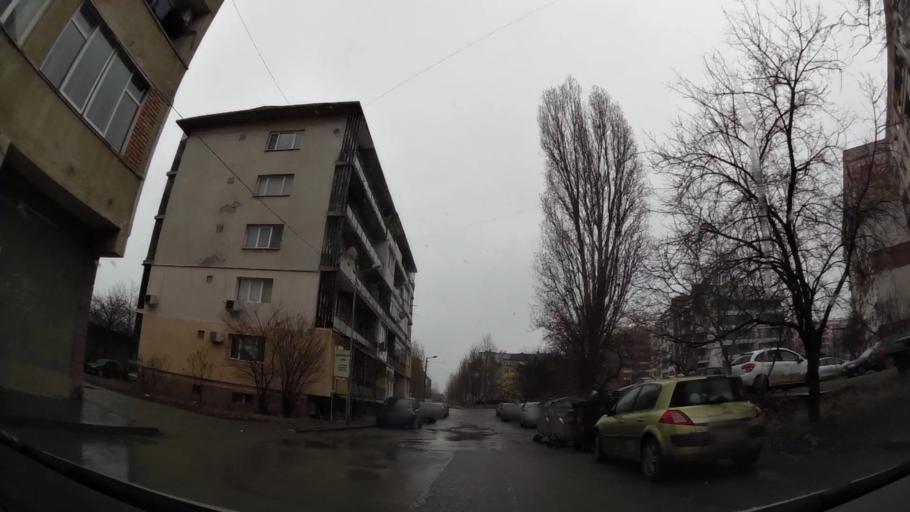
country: BG
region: Sofia-Capital
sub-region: Stolichna Obshtina
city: Sofia
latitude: 42.6650
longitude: 23.3822
